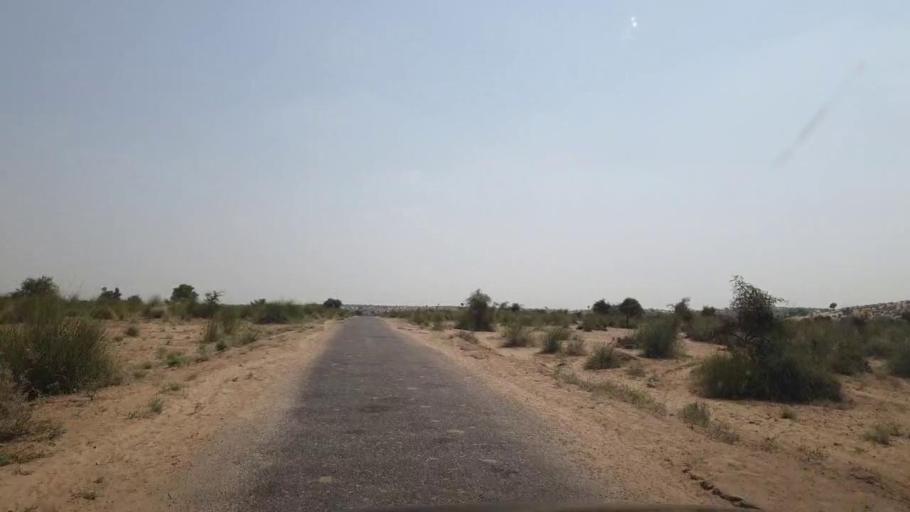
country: PK
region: Sindh
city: Islamkot
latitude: 25.0750
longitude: 70.7409
